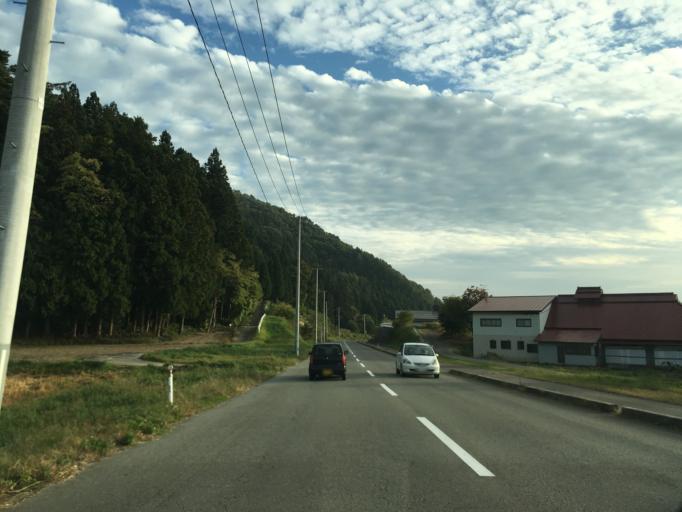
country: JP
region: Fukushima
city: Inawashiro
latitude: 37.5335
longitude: 140.1462
